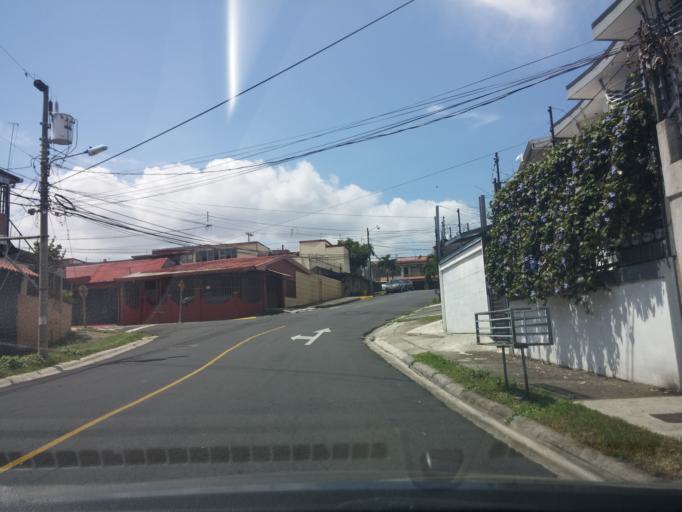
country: CR
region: Heredia
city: San Francisco
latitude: 9.9925
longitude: -84.1406
